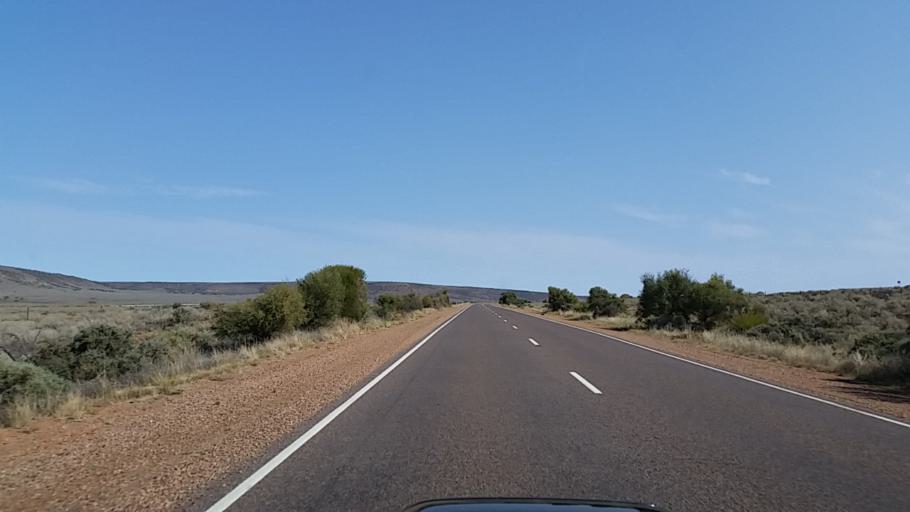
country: AU
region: South Australia
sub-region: Port Augusta
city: Port Augusta West
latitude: -32.5748
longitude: 137.6239
